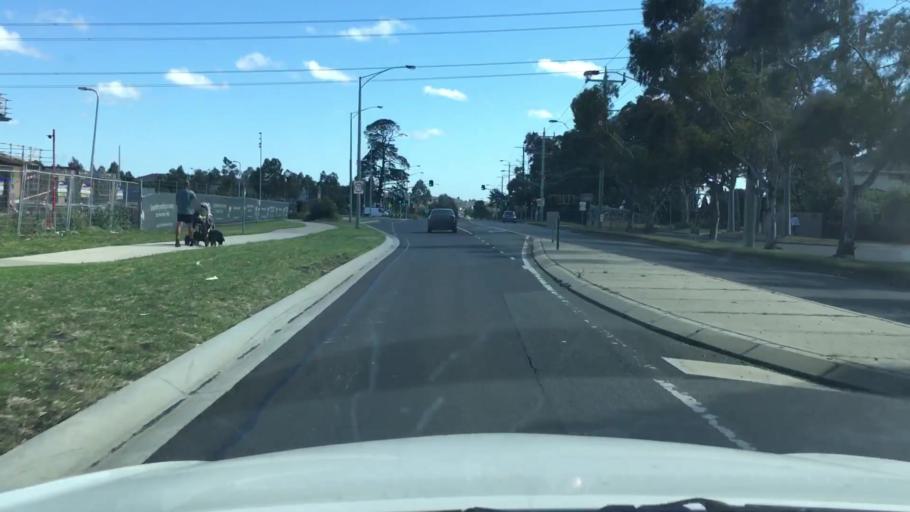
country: AU
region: Victoria
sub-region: Monash
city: Mulgrave
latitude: -37.9312
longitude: 145.1938
